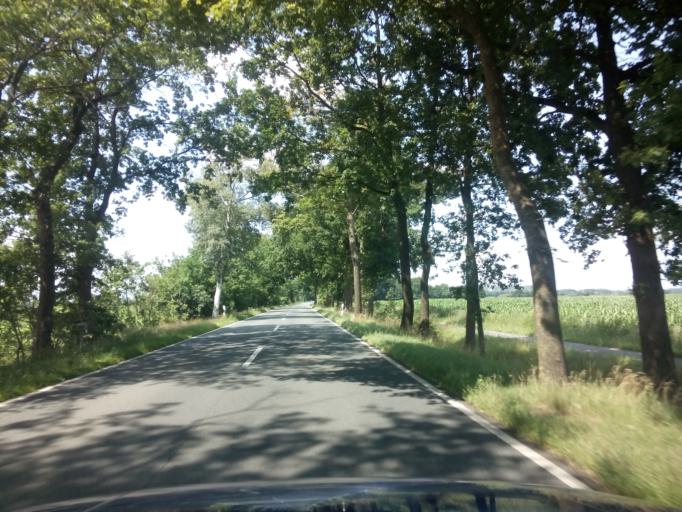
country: DE
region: Lower Saxony
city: Worpswede
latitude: 53.2567
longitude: 8.9388
